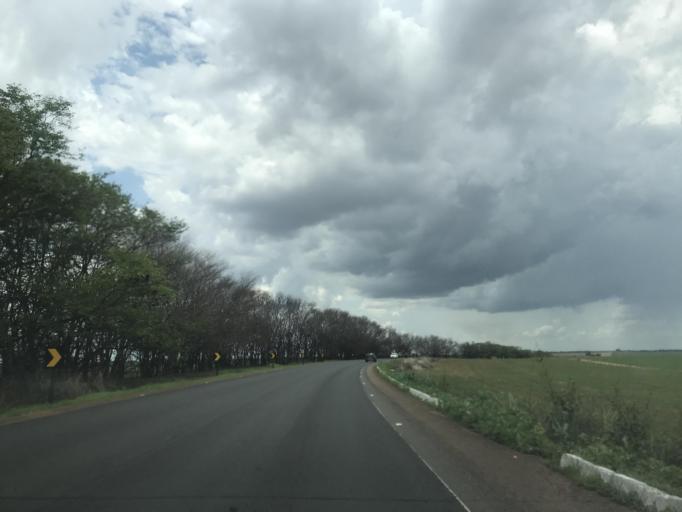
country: BR
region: Goias
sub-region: Vianopolis
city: Vianopolis
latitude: -16.8066
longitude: -48.5187
